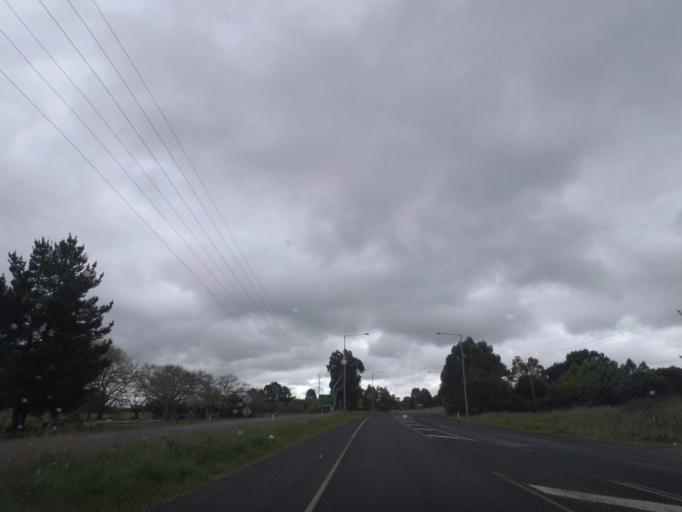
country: AU
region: Victoria
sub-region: Hume
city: Sunbury
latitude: -37.3241
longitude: 144.5237
